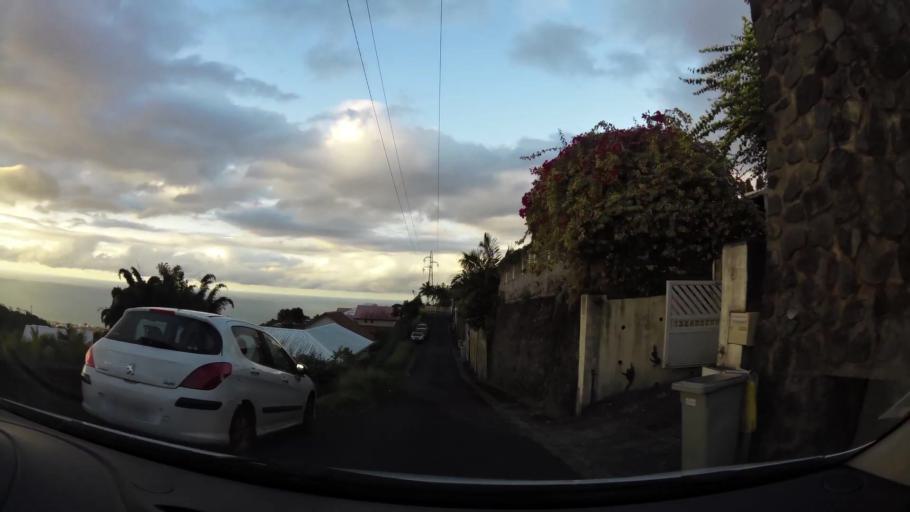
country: RE
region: Reunion
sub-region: Reunion
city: Saint-Denis
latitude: -20.9198
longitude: 55.4647
